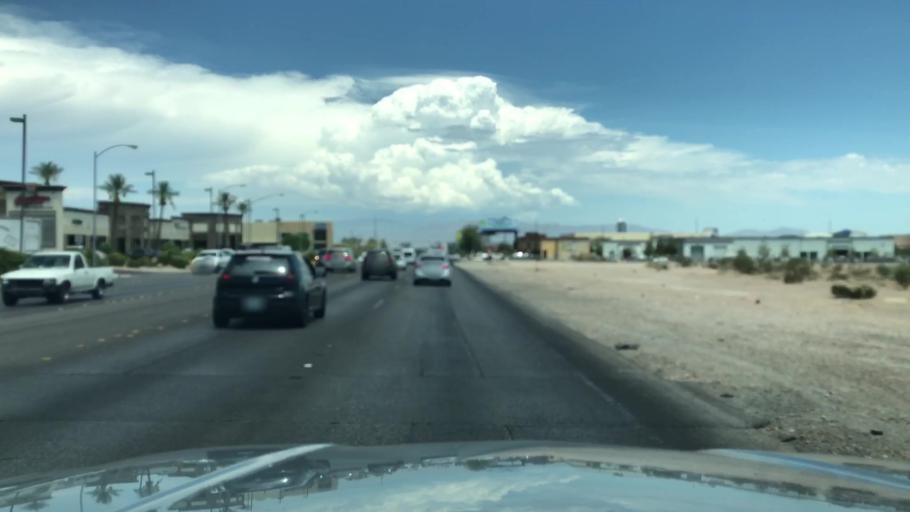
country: US
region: Nevada
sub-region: Clark County
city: Spring Valley
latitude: 36.0808
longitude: -115.2078
